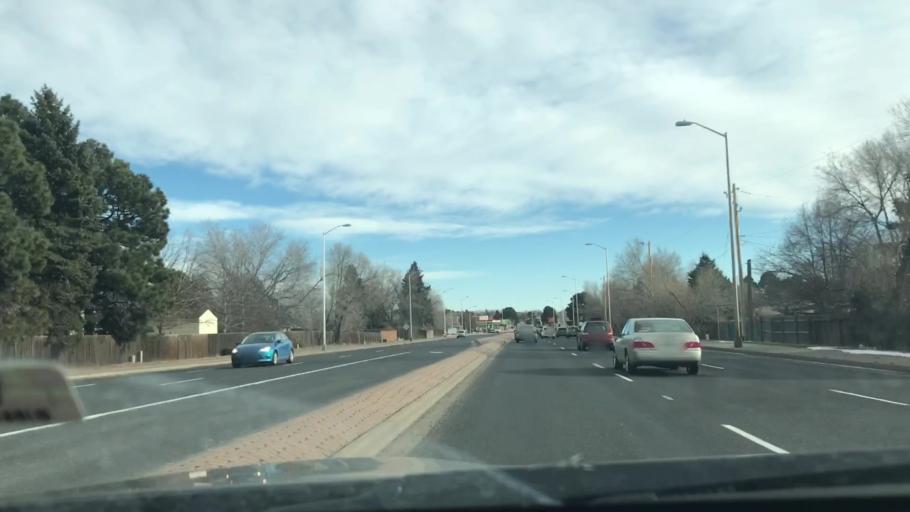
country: US
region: Colorado
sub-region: El Paso County
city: Cimarron Hills
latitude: 38.8969
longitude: -104.7611
